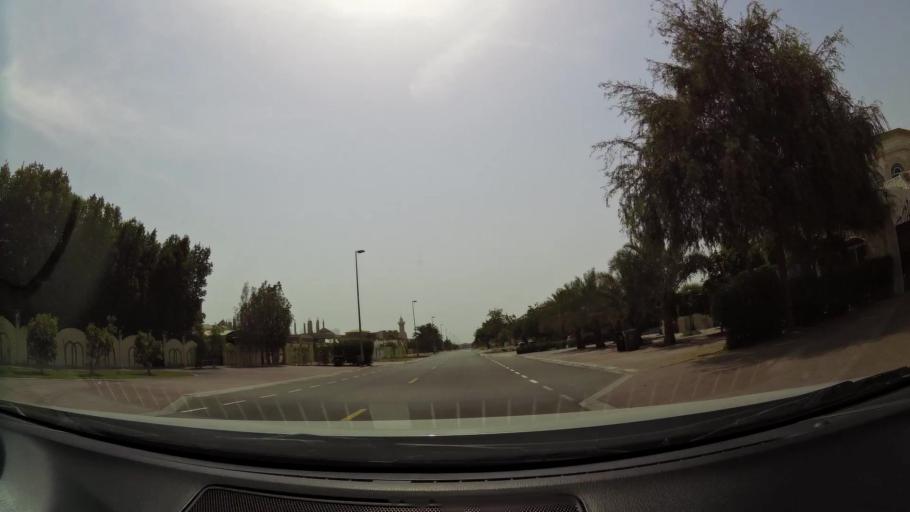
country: AE
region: Ash Shariqah
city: Sharjah
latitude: 25.2381
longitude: 55.4481
